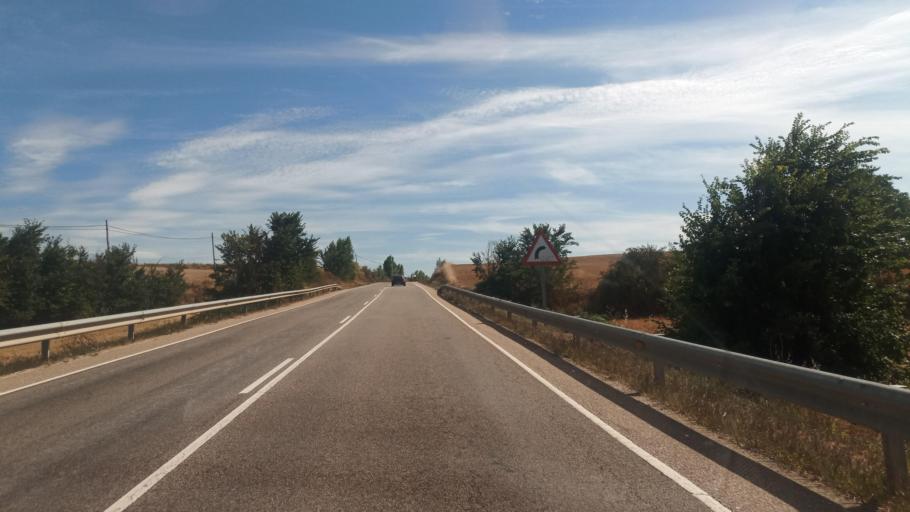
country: ES
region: Castille and Leon
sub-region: Provincia de Burgos
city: Aguilar de Bureba
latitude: 42.5744
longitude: -3.3322
